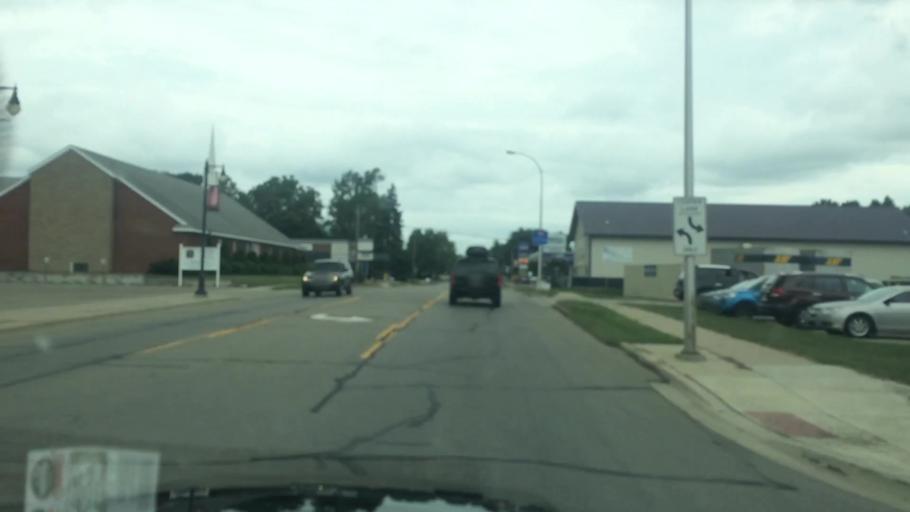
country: US
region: Michigan
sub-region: Sanilac County
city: Marlette
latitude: 43.3287
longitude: -83.0798
